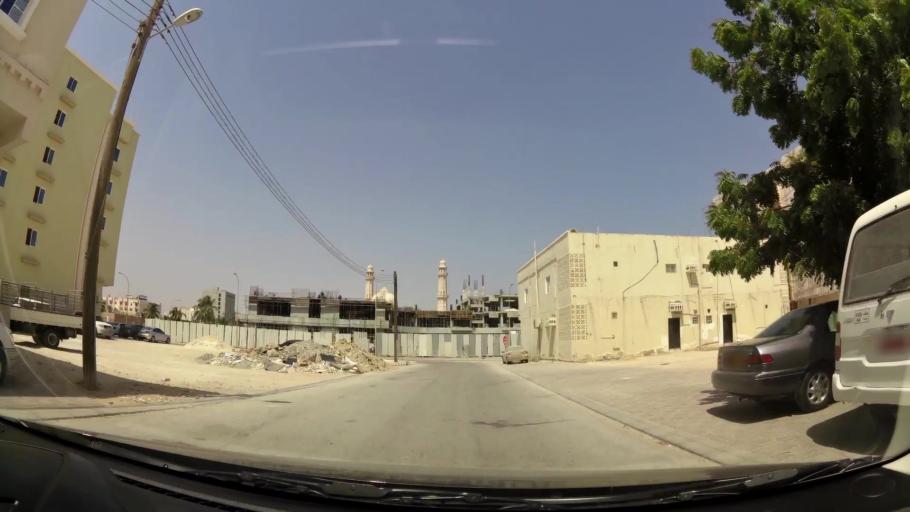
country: OM
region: Zufar
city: Salalah
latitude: 17.0168
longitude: 54.0911
